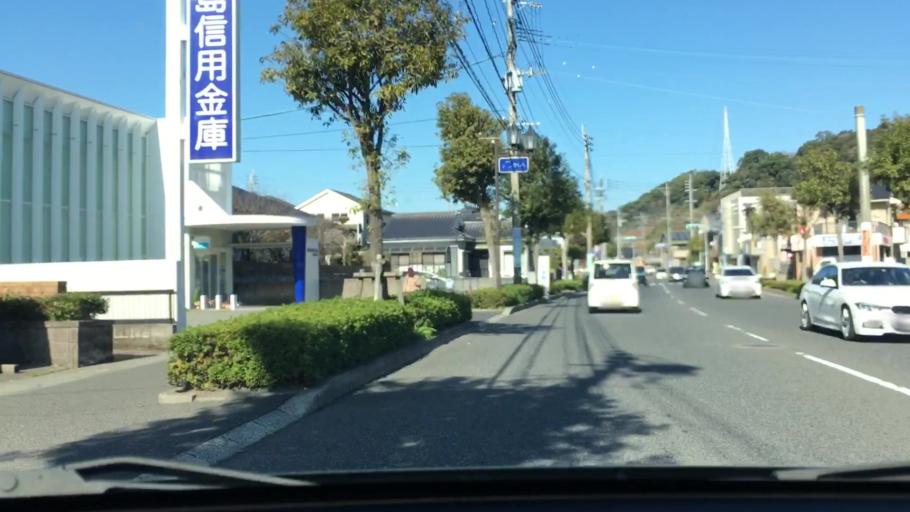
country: JP
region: Kagoshima
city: Kagoshima-shi
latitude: 31.5468
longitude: 130.5335
